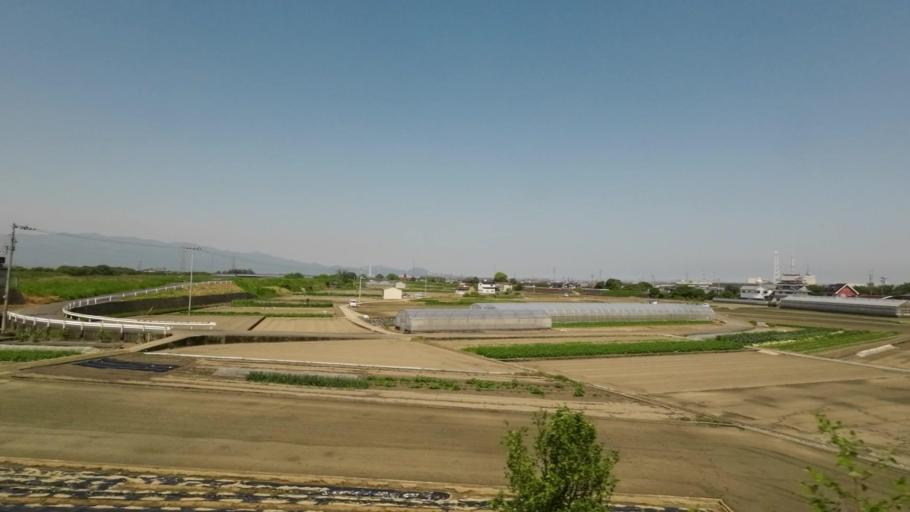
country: JP
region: Ehime
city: Saijo
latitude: 33.9073
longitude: 133.1808
